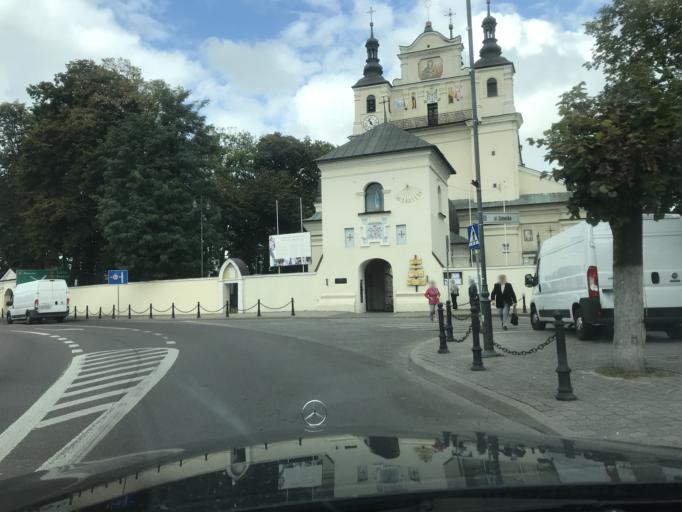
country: PL
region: Lublin Voivodeship
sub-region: Powiat janowski
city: Janow Lubelski
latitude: 50.7071
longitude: 22.4101
